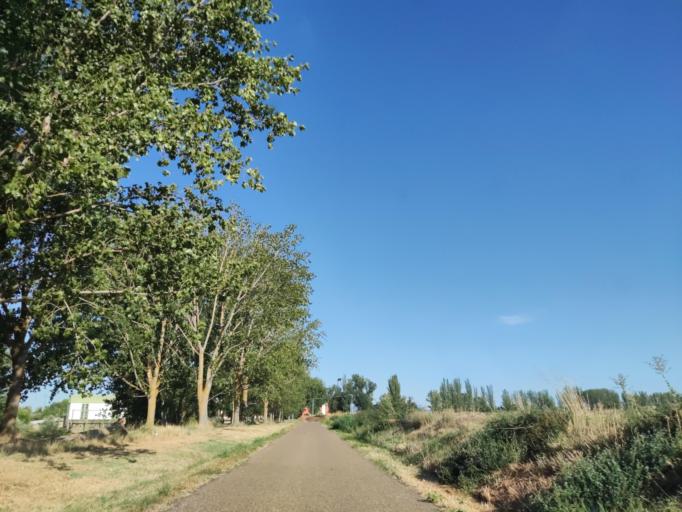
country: ES
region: Castille and Leon
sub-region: Provincia de Zamora
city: Villaralbo
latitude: 41.5023
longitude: -5.6896
